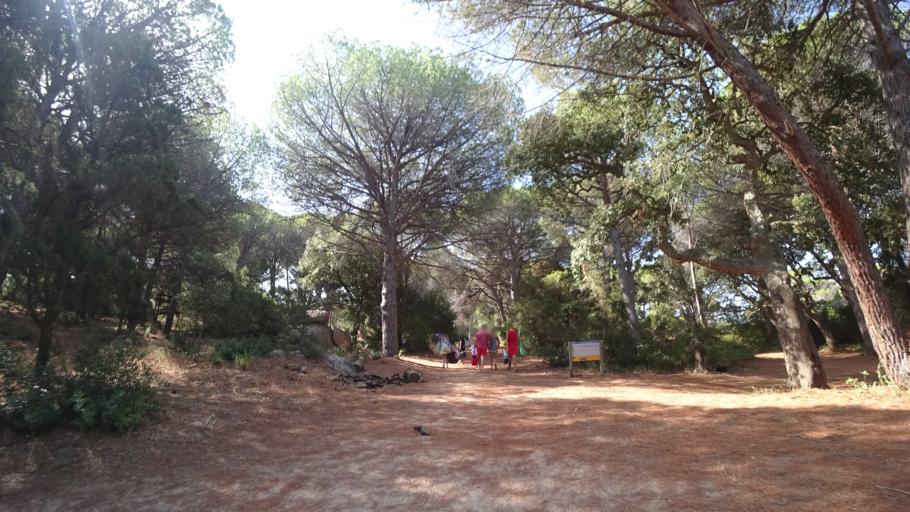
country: FR
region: Corsica
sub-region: Departement de la Corse-du-Sud
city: Porto-Vecchio
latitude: 41.5610
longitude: 9.3370
